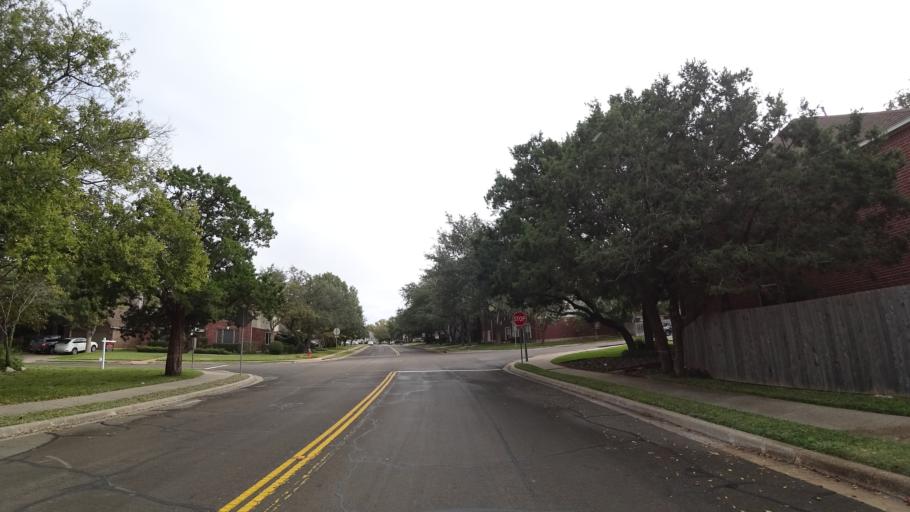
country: US
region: Texas
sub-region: Williamson County
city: Brushy Creek
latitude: 30.5178
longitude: -97.7156
